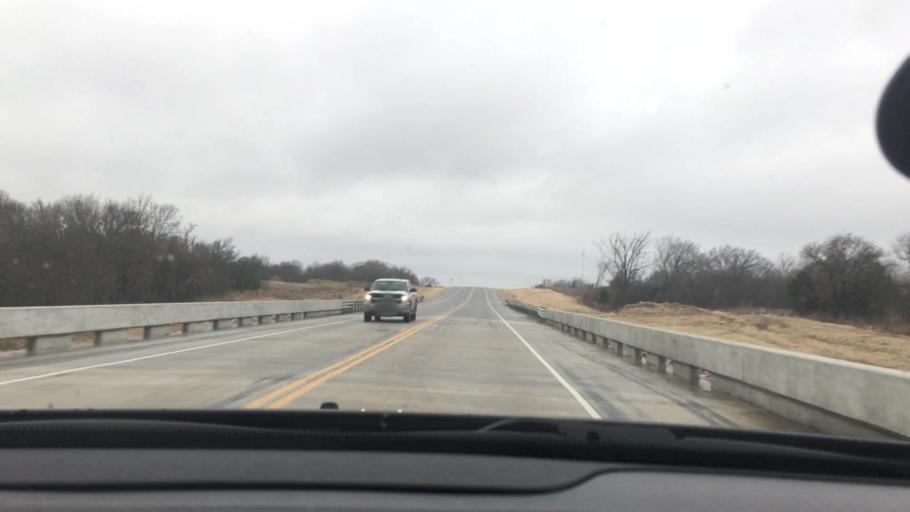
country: US
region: Oklahoma
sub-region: Johnston County
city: Tishomingo
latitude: 34.3296
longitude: -96.6577
